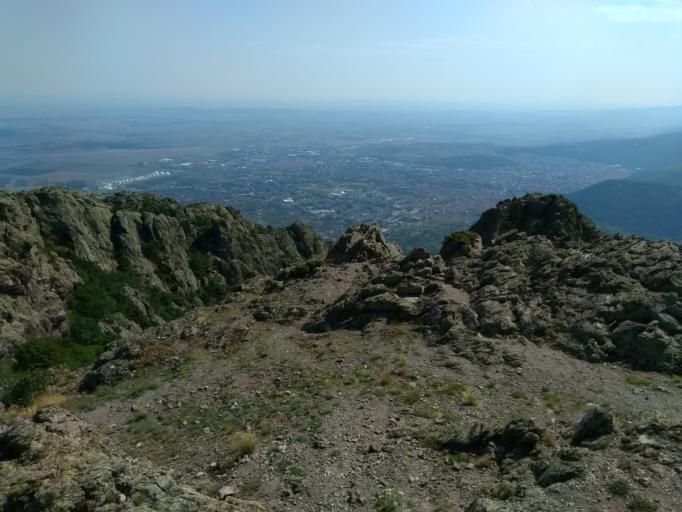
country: BG
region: Sliven
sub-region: Obshtina Sliven
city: Sliven
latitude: 42.7150
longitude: 26.3620
